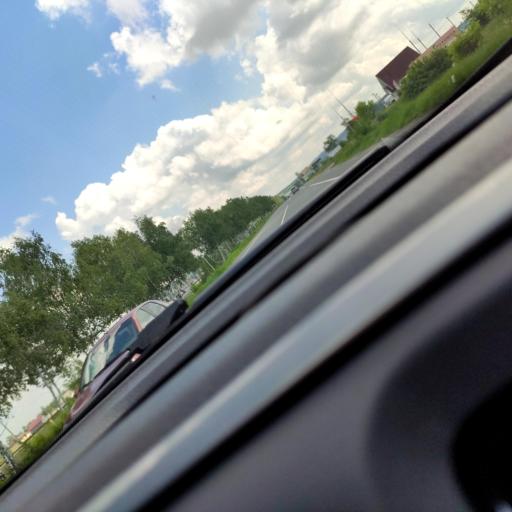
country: RU
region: Samara
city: Kurumoch
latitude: 53.4866
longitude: 50.0099
